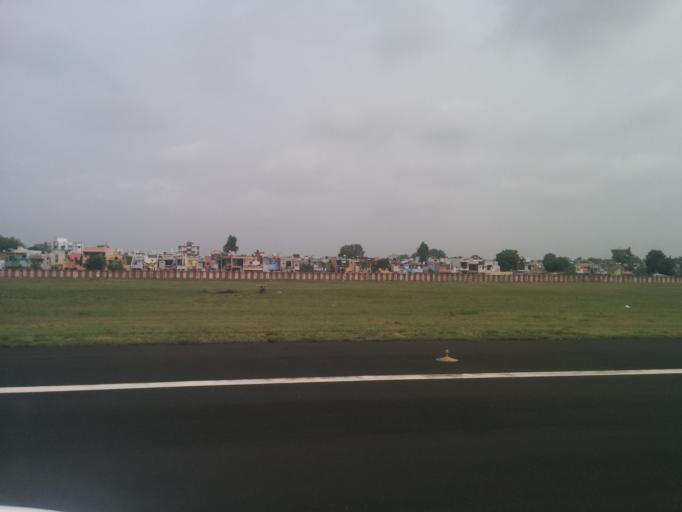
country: IN
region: Gujarat
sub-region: Ahmadabad
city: Naroda
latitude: 23.0792
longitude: 72.6365
